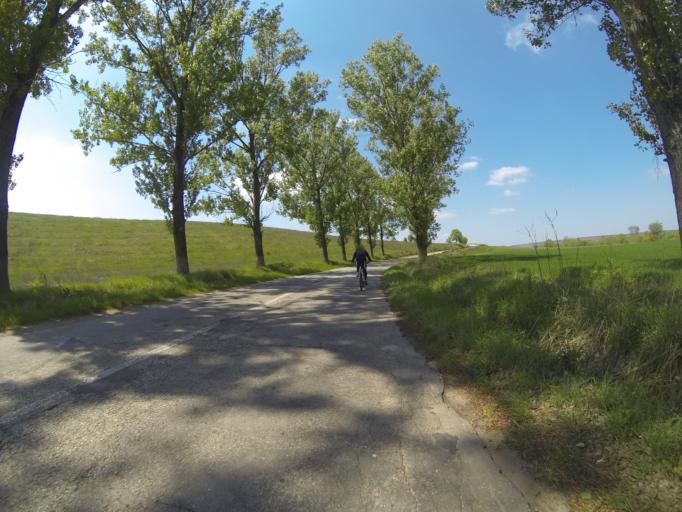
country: RO
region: Dolj
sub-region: Comuna Salcuta
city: Salcuta
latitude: 44.2561
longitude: 23.4510
